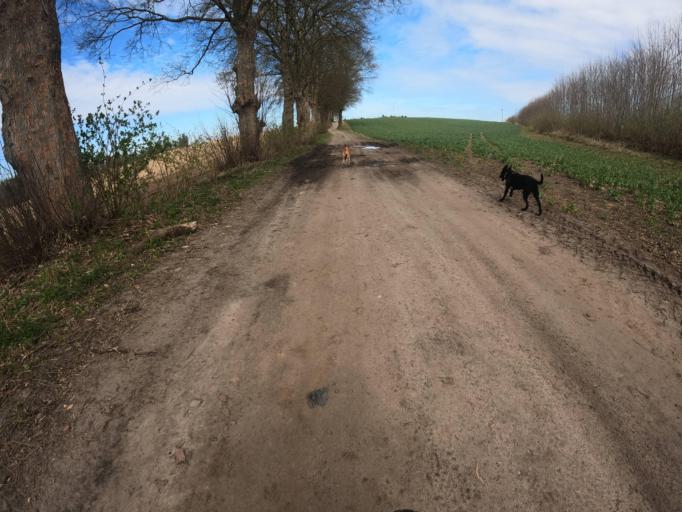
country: PL
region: West Pomeranian Voivodeship
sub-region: Powiat gryficki
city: Brojce
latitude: 53.9646
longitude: 15.3751
